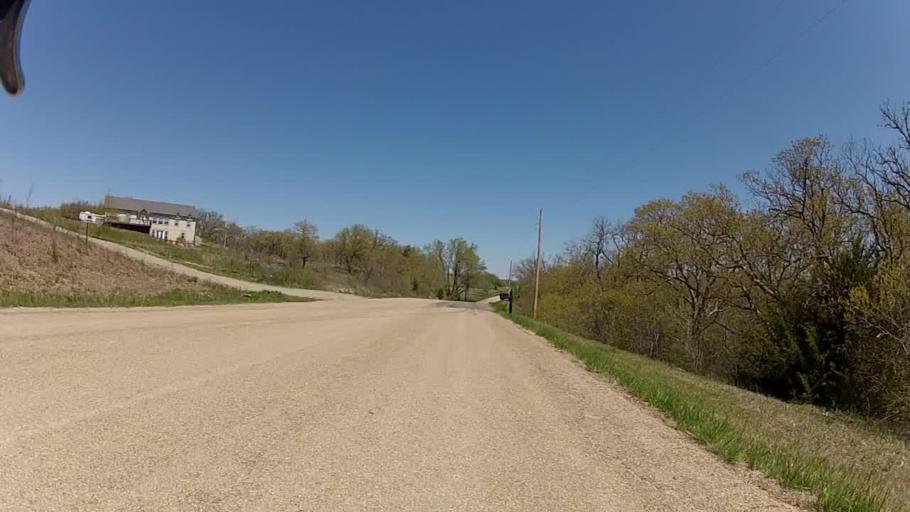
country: US
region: Kansas
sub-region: Riley County
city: Ogden
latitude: 38.9913
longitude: -96.5973
